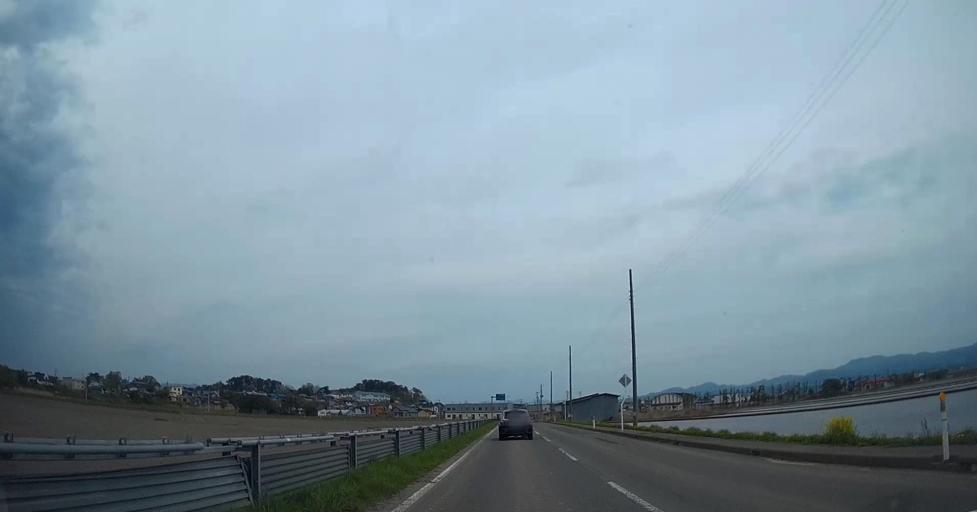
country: JP
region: Aomori
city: Shimokizukuri
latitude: 40.9756
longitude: 140.3690
